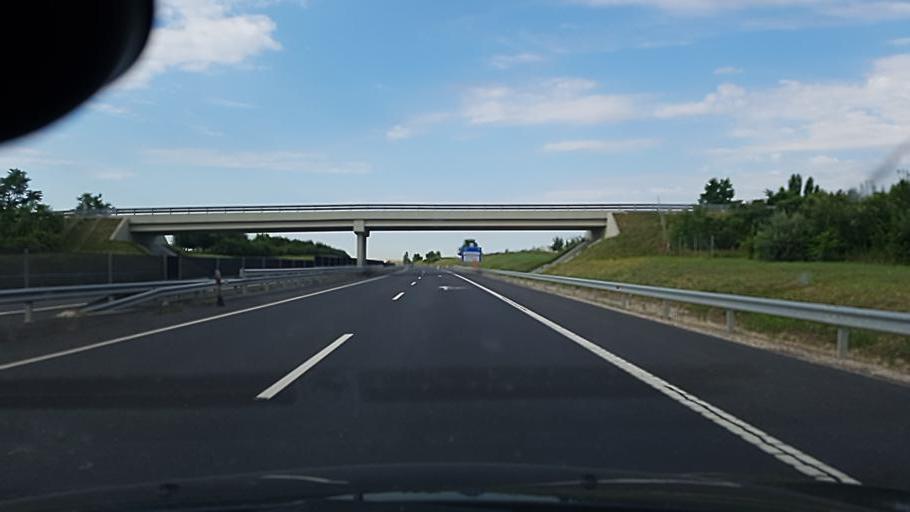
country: HU
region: Pest
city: Szazhalombatta
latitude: 47.3146
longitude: 18.8698
